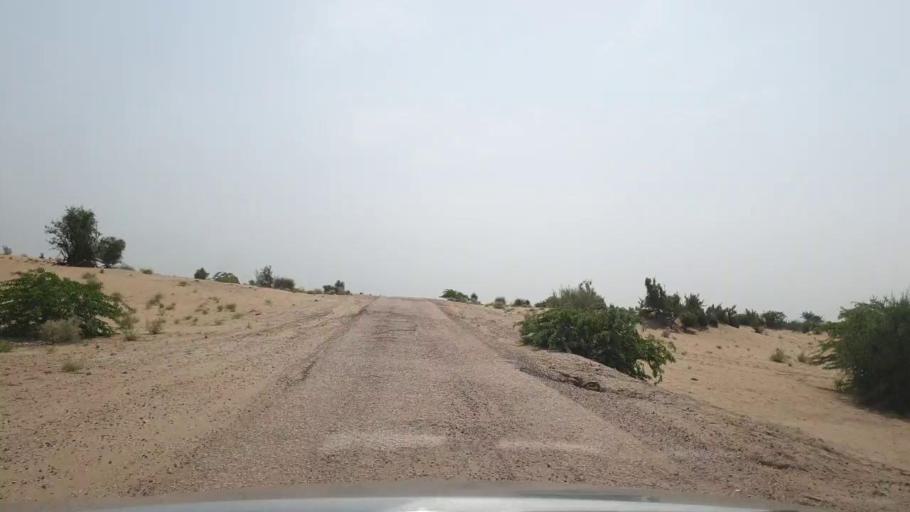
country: PK
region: Sindh
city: Pano Aqil
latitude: 27.6172
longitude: 69.1236
